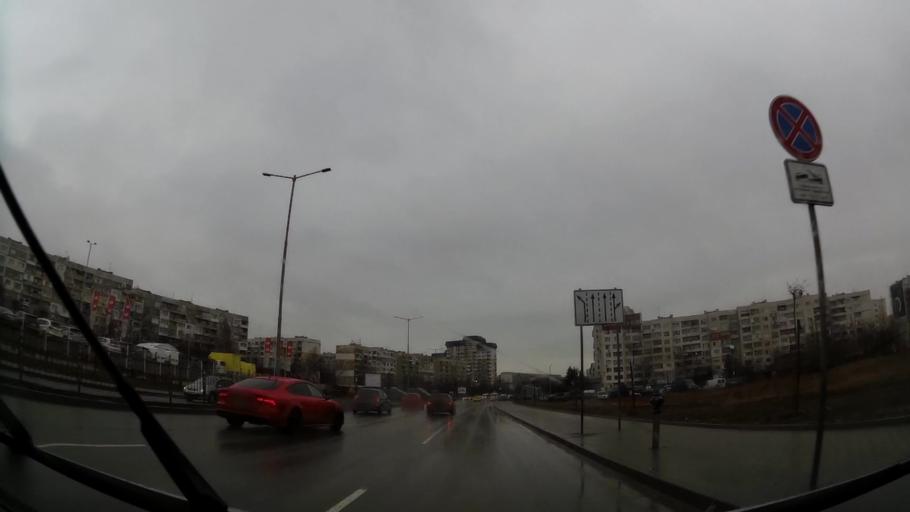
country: BG
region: Sofia-Capital
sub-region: Stolichna Obshtina
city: Sofia
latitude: 42.6399
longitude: 23.3730
